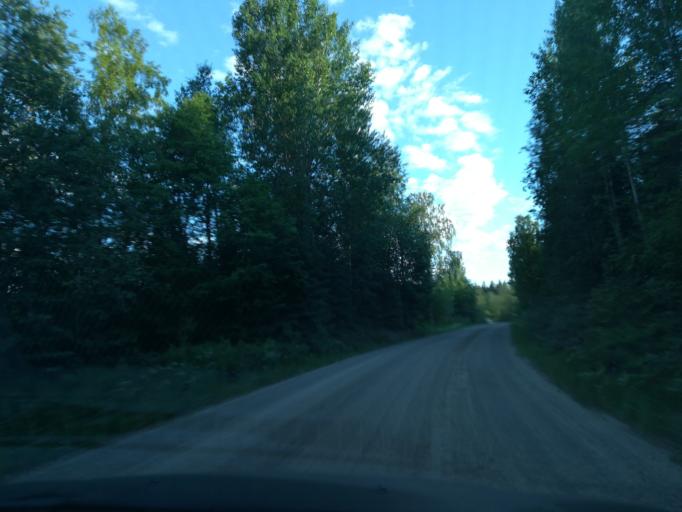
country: FI
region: Southern Savonia
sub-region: Mikkeli
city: Puumala
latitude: 61.5975
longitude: 28.1181
